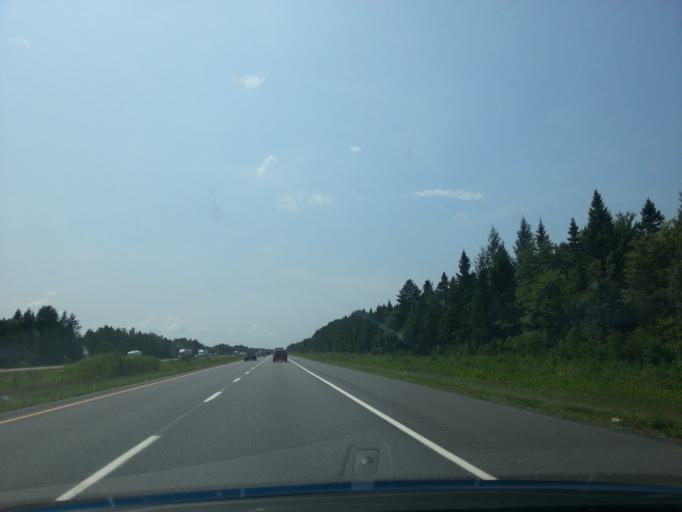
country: CA
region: Quebec
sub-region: Mauricie
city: Princeville
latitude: 46.2938
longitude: -71.9767
